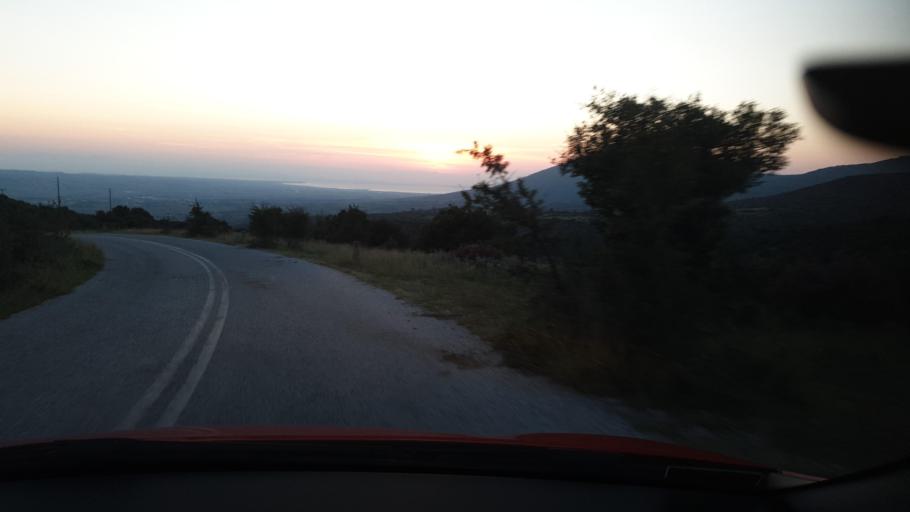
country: GR
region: Central Macedonia
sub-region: Nomos Thessalonikis
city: Peristera
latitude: 40.5167
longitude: 23.1776
